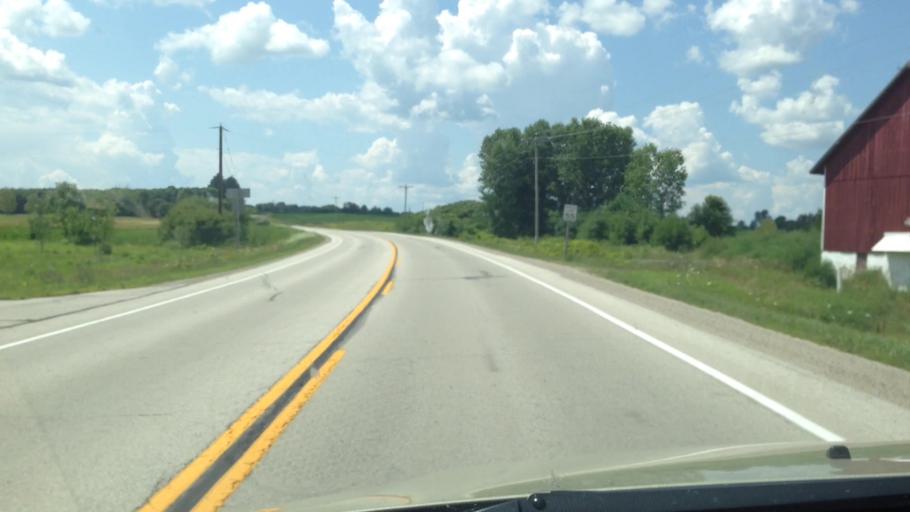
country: US
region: Wisconsin
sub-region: Brown County
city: Suamico
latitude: 44.6481
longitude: -88.1224
